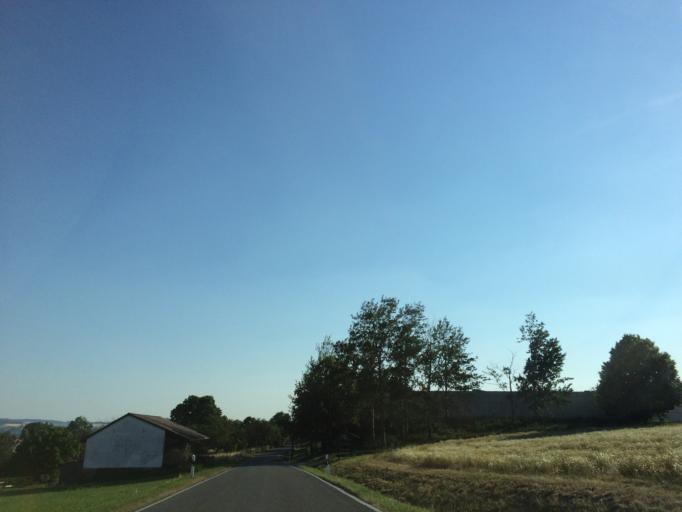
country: DE
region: Thuringia
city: Gossitz
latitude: 50.6254
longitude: 11.5893
